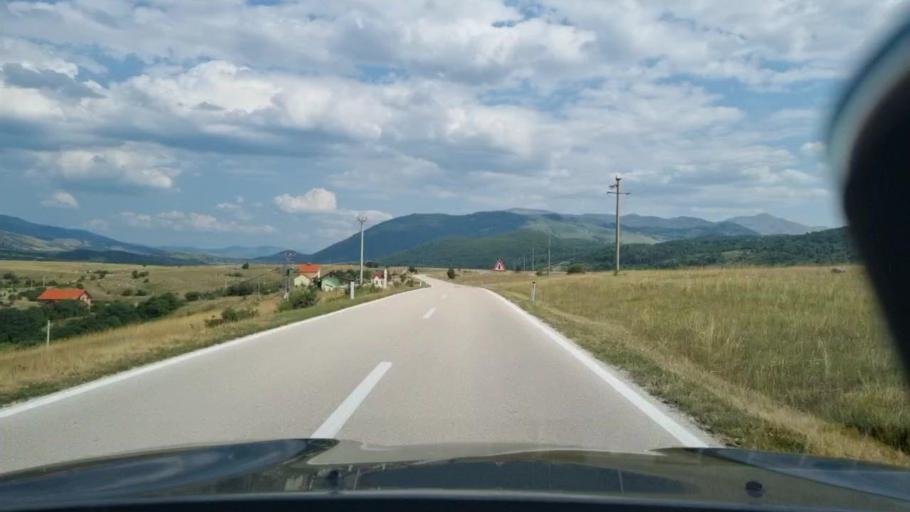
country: BA
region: Federation of Bosnia and Herzegovina
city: Bosansko Grahovo
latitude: 44.1542
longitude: 16.4359
